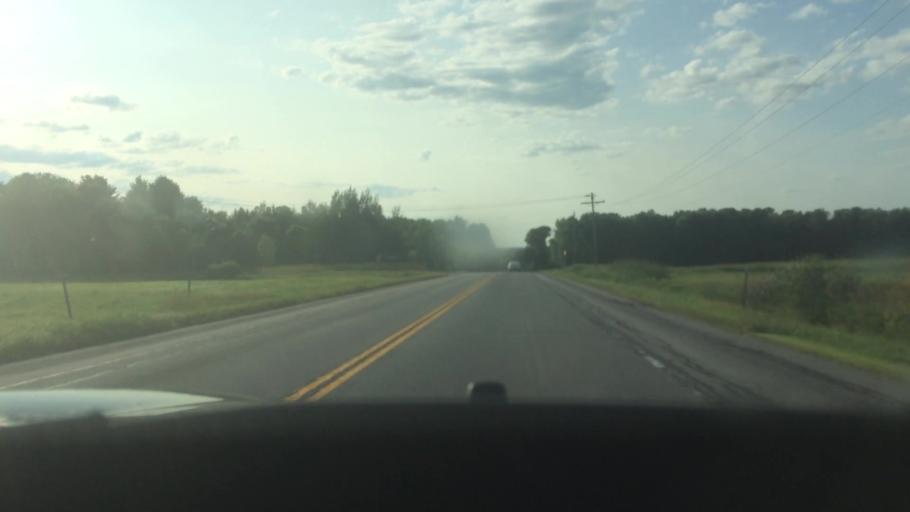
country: US
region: New York
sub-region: St. Lawrence County
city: Canton
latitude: 44.6034
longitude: -75.2019
